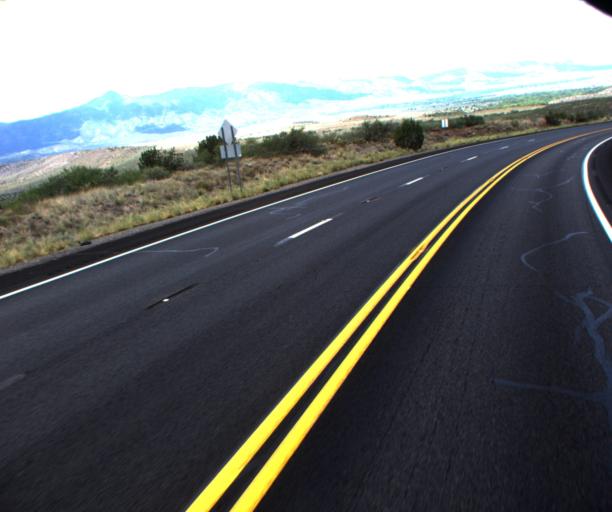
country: US
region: Arizona
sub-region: Yavapai County
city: Camp Verde
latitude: 34.5087
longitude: -111.7396
